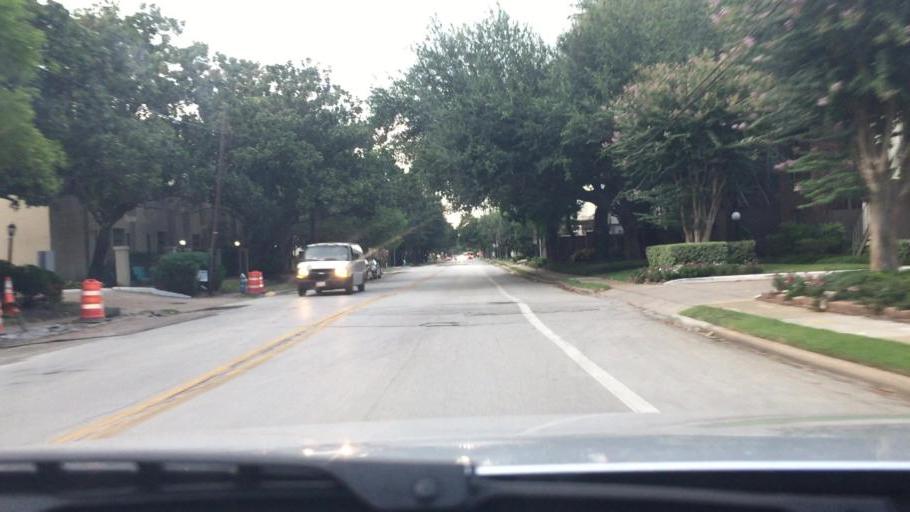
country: US
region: Texas
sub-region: Harris County
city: Hunters Creek Village
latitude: 29.7533
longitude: -95.4796
